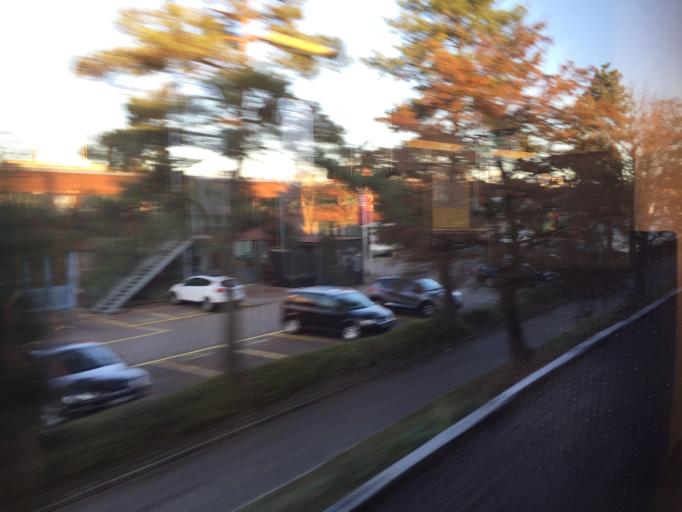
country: CH
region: Zug
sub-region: Zug
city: Zug
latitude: 47.1864
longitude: 8.5174
